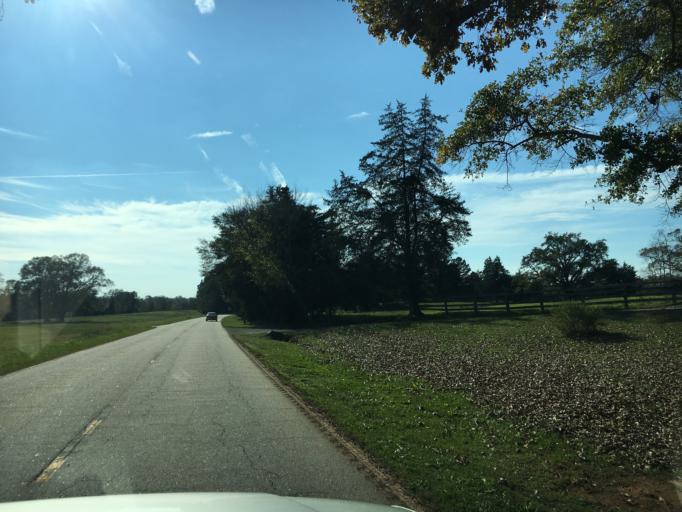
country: US
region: South Carolina
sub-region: Anderson County
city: Iva
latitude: 34.3540
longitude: -82.7287
